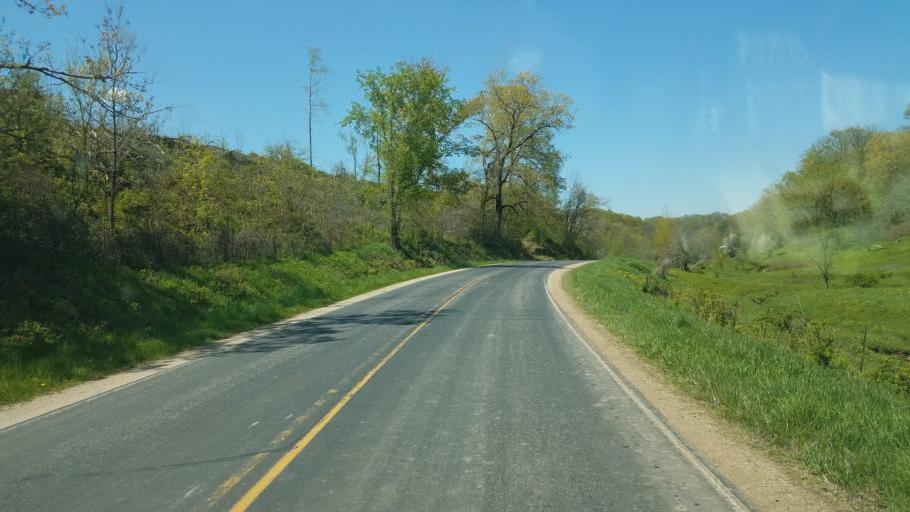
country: US
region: Wisconsin
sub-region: Vernon County
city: Hillsboro
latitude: 43.5774
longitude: -90.3694
